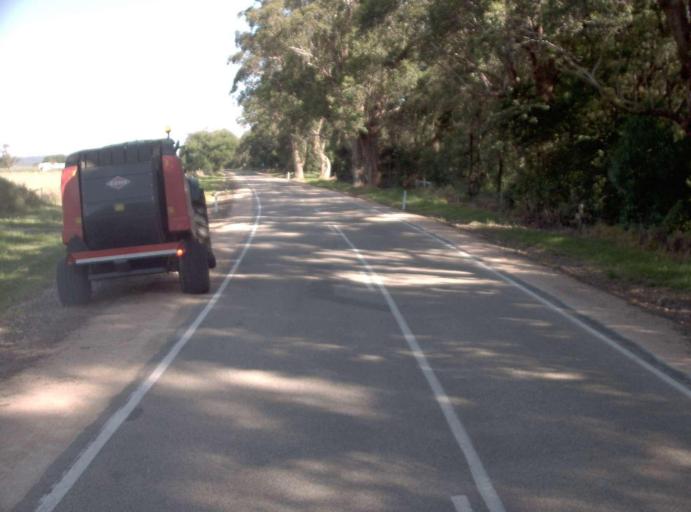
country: AU
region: Victoria
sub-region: East Gippsland
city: Lakes Entrance
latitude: -37.7388
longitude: 148.5057
